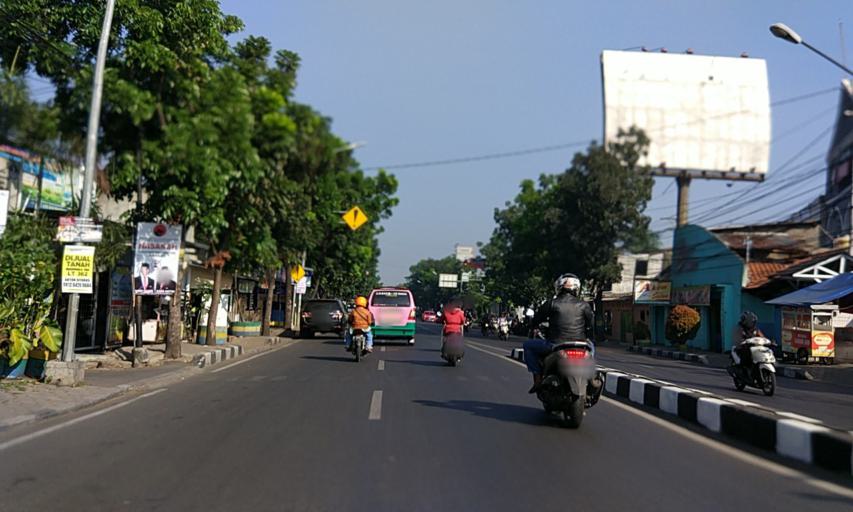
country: ID
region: West Java
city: Bandung
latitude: -6.9019
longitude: 107.6533
